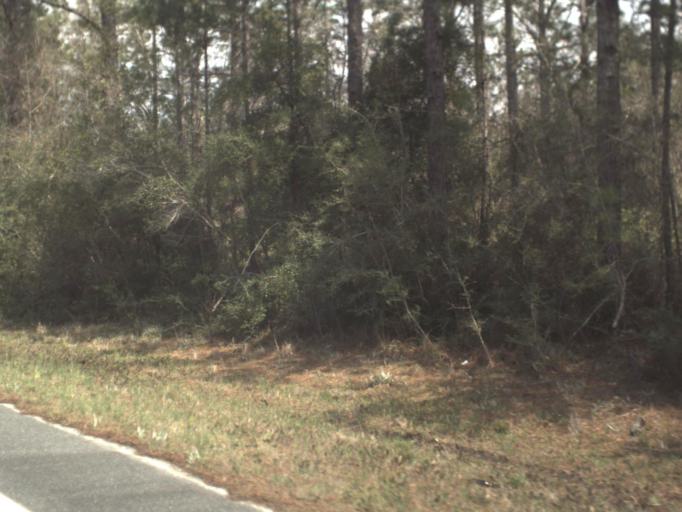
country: US
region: Florida
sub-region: Franklin County
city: Apalachicola
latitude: 29.9238
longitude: -84.9772
